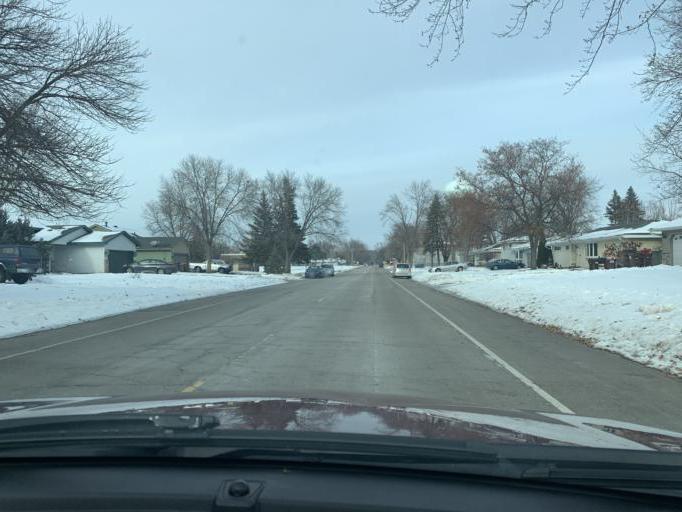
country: US
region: Minnesota
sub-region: Washington County
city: Saint Paul Park
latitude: 44.8321
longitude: -92.9841
